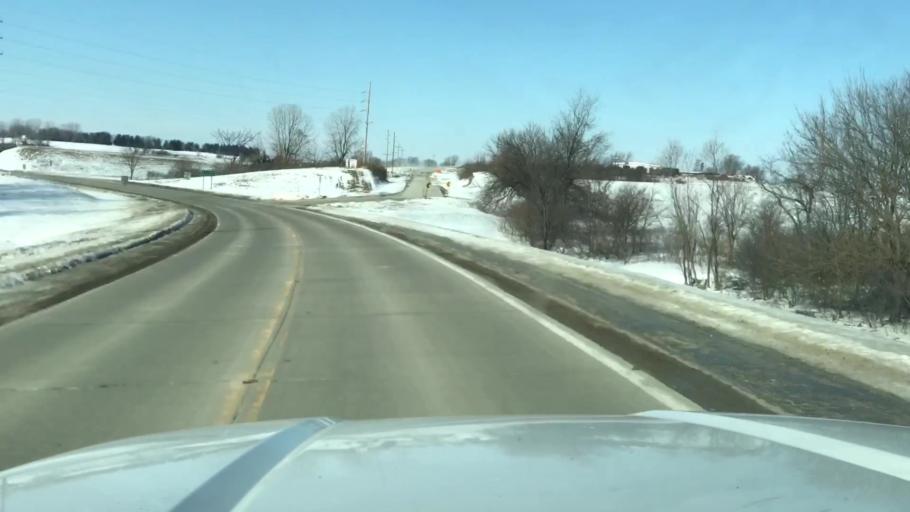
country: US
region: Missouri
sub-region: Andrew County
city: Savannah
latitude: 39.9615
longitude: -94.8575
